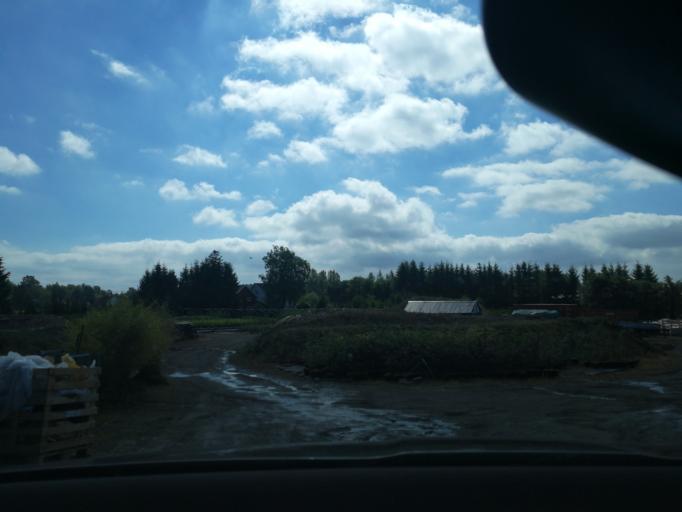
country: NO
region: Vestfold
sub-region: Sandefjord
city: Sandefjord
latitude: 59.1526
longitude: 10.1970
